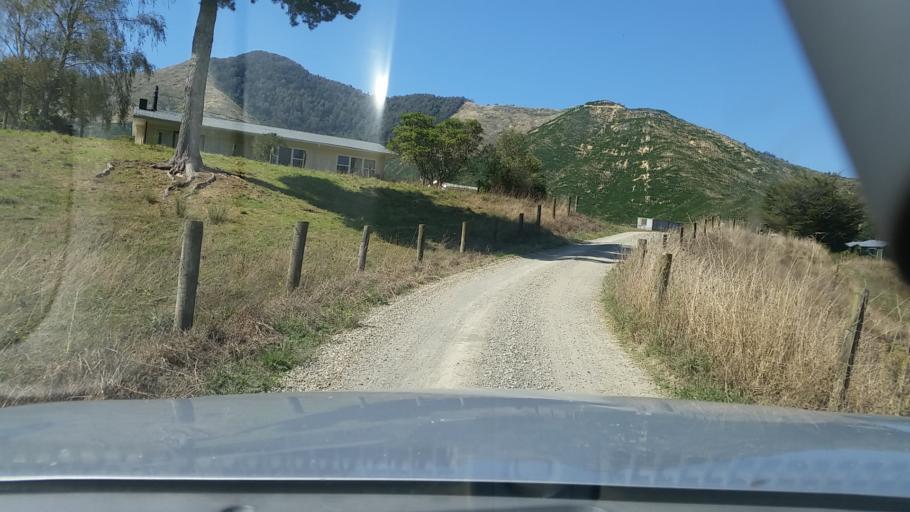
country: NZ
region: Nelson
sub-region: Nelson City
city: Nelson
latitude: -41.2710
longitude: 173.5792
